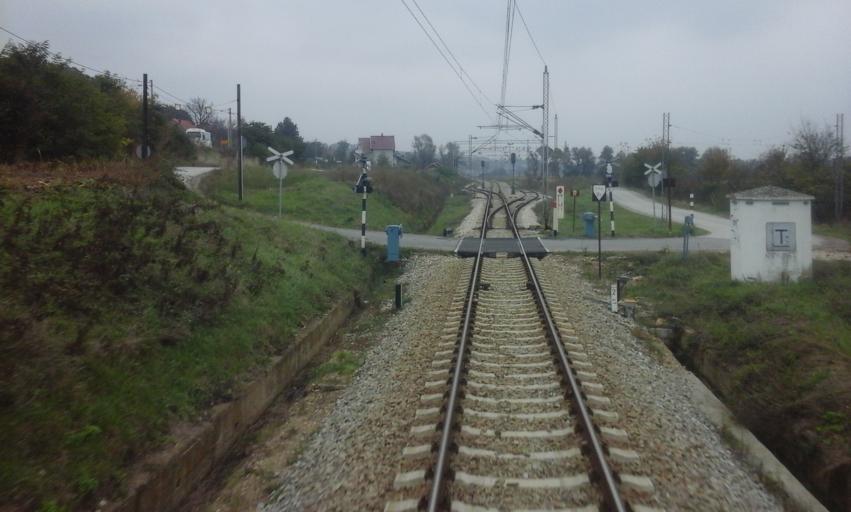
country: RS
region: Central Serbia
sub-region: Belgrade
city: Mladenovac
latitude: 44.4852
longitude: 20.6569
